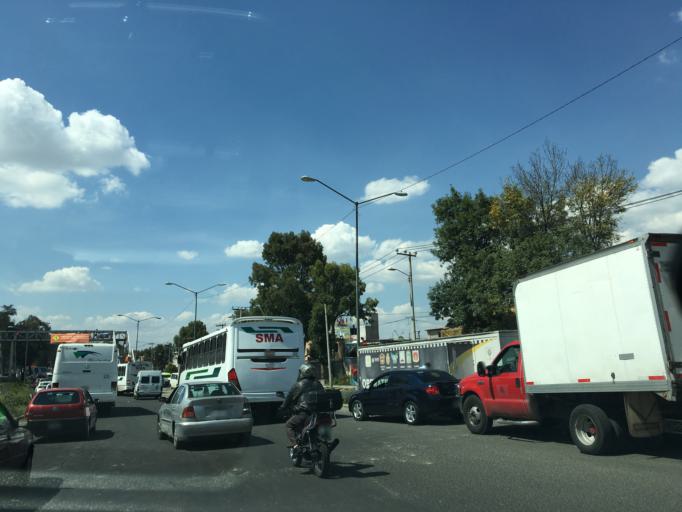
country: MX
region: Mexico
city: Los Reyes La Paz
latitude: 19.3608
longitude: -98.9994
